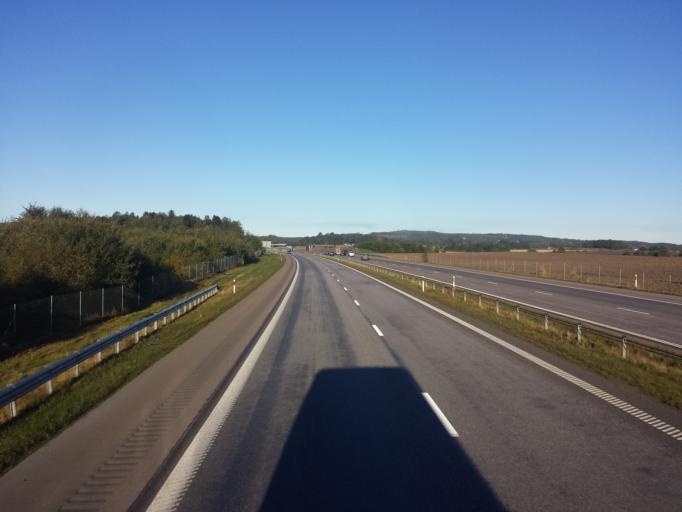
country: SE
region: Halland
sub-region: Halmstads Kommun
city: Getinge
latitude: 56.8036
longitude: 12.7576
